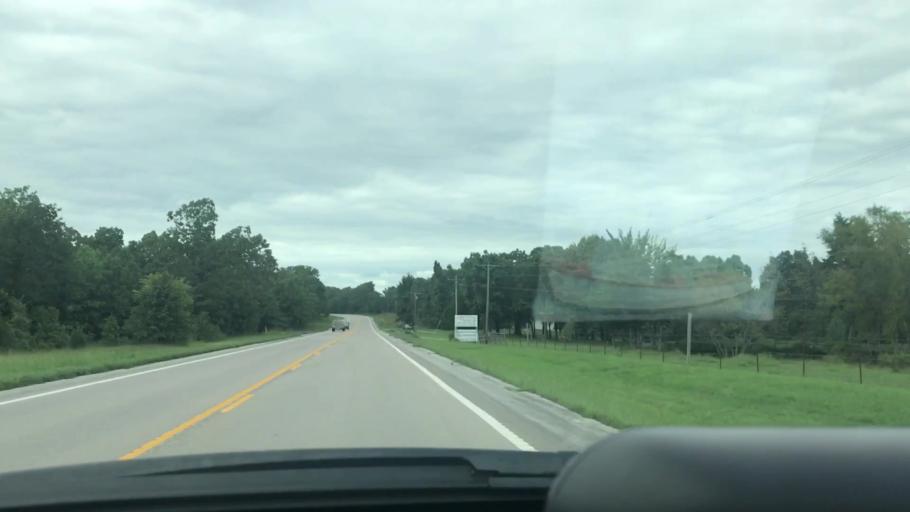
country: US
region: Missouri
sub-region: Benton County
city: Warsaw
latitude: 38.1556
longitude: -93.2967
